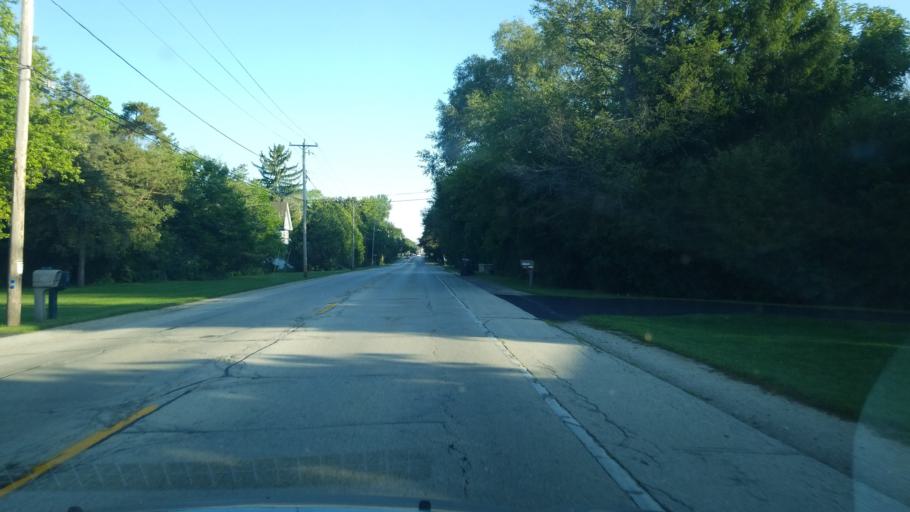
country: US
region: Wisconsin
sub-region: Ozaukee County
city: Mequon
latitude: 43.2132
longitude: -87.9771
